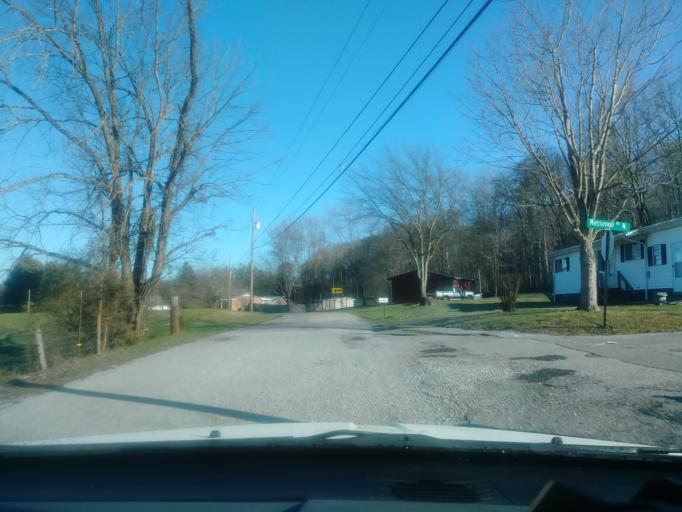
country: US
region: Tennessee
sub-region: Greene County
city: Mosheim
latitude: 36.1096
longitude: -82.9294
